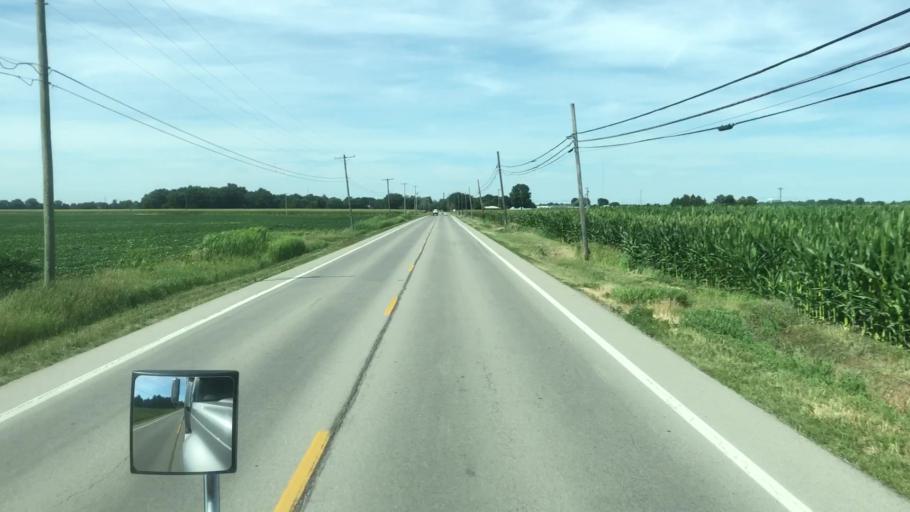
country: US
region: Ohio
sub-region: Sandusky County
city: Fremont
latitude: 41.3743
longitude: -83.0657
